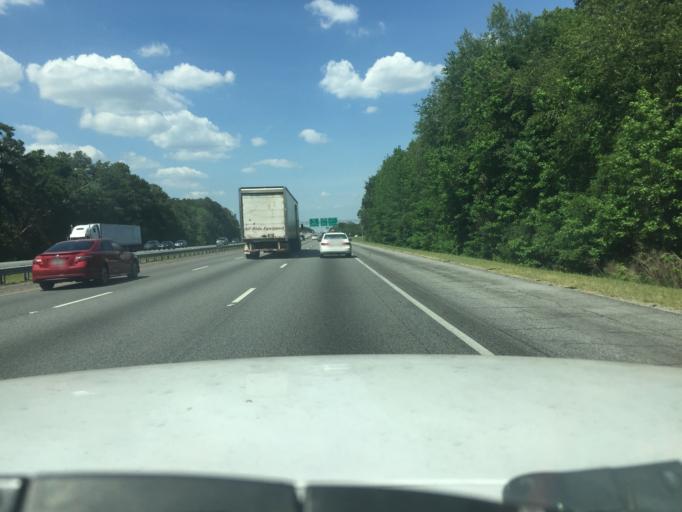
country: US
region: Georgia
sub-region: Chatham County
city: Pooler
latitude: 32.0674
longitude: -81.2493
